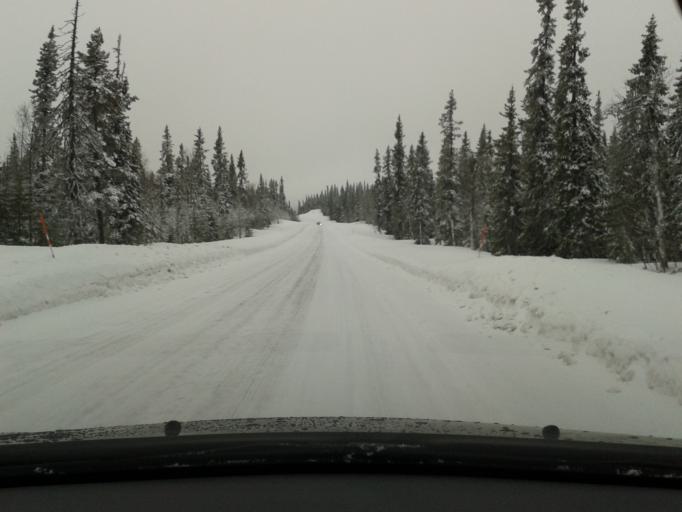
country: SE
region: Vaesterbotten
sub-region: Vilhelmina Kommun
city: Sjoberg
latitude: 65.1108
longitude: 15.8778
